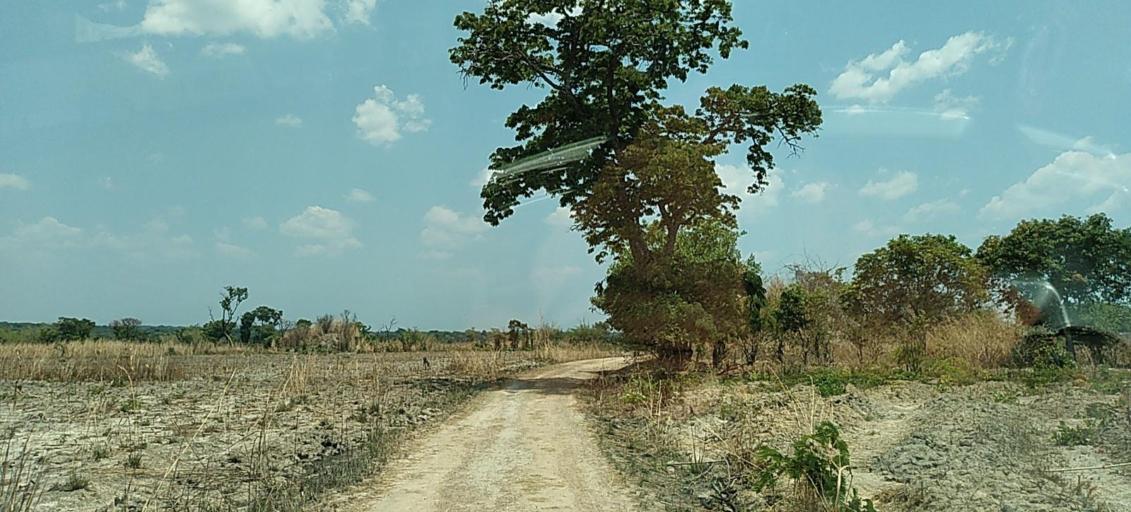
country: ZM
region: Copperbelt
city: Chililabombwe
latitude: -12.4815
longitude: 27.6681
